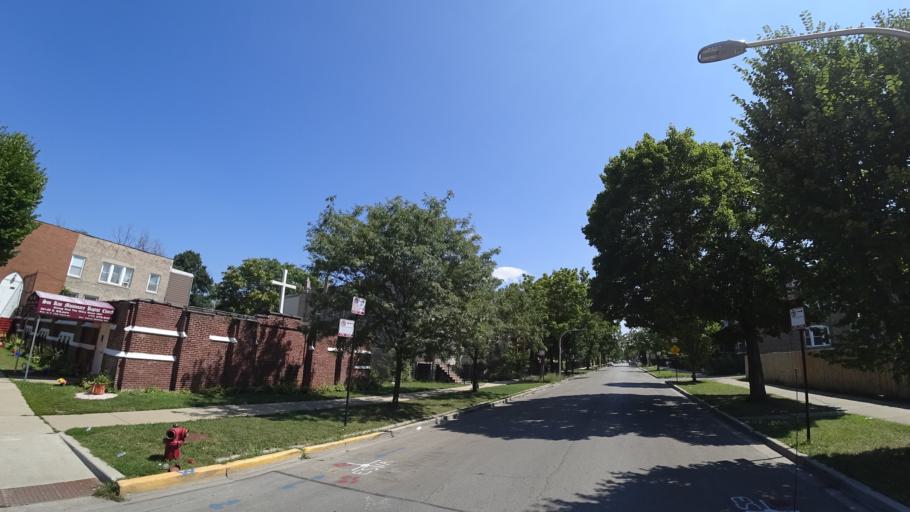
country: US
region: Illinois
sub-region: Cook County
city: Cicero
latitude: 41.8750
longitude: -87.7377
